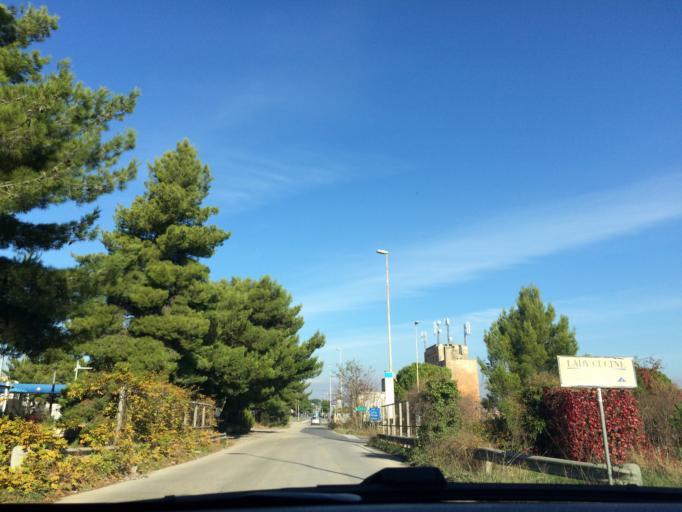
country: IT
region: Basilicate
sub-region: Provincia di Matera
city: Matera
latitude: 40.6814
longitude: 16.5902
